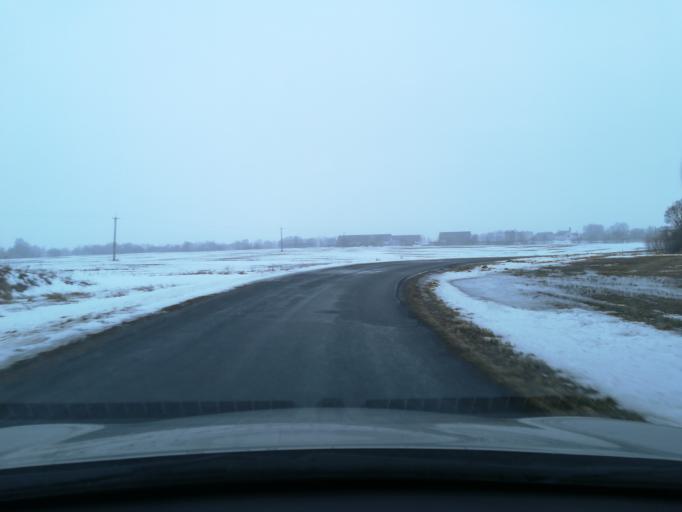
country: EE
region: Harju
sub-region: Raasiku vald
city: Raasiku
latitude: 59.3513
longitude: 25.2067
